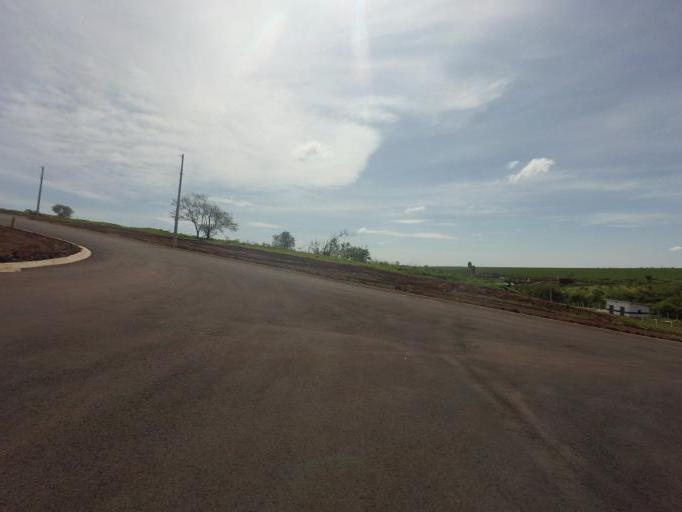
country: BR
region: Sao Paulo
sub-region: Piracicaba
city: Piracicaba
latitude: -22.7630
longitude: -47.5798
